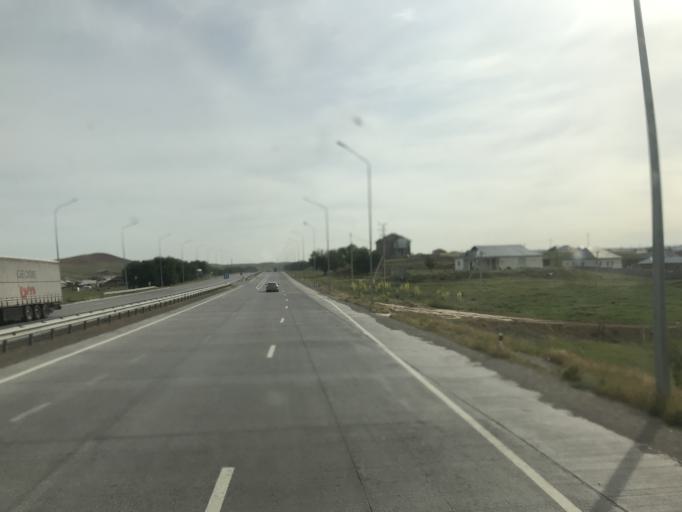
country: KZ
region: Ongtustik Qazaqstan
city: Shymkent
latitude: 42.2115
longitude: 69.5196
